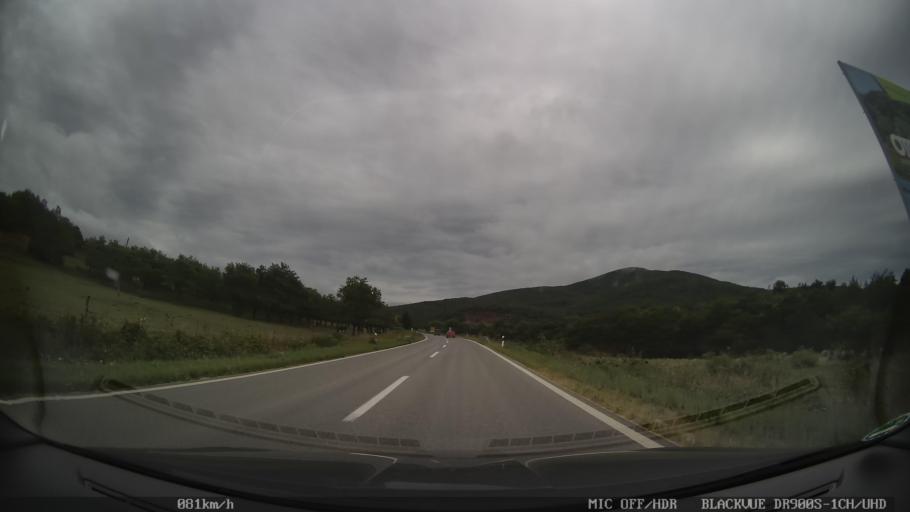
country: HR
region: Licko-Senjska
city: Otocac
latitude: 44.8562
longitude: 15.3293
